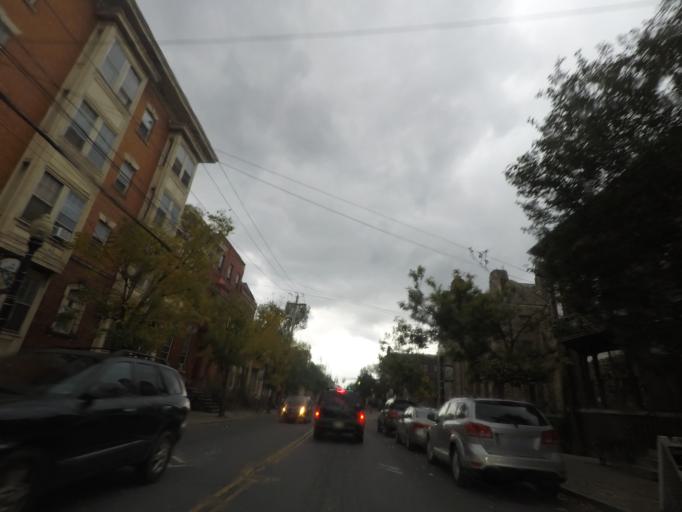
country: US
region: New York
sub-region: Albany County
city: Albany
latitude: 42.6554
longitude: -73.7648
